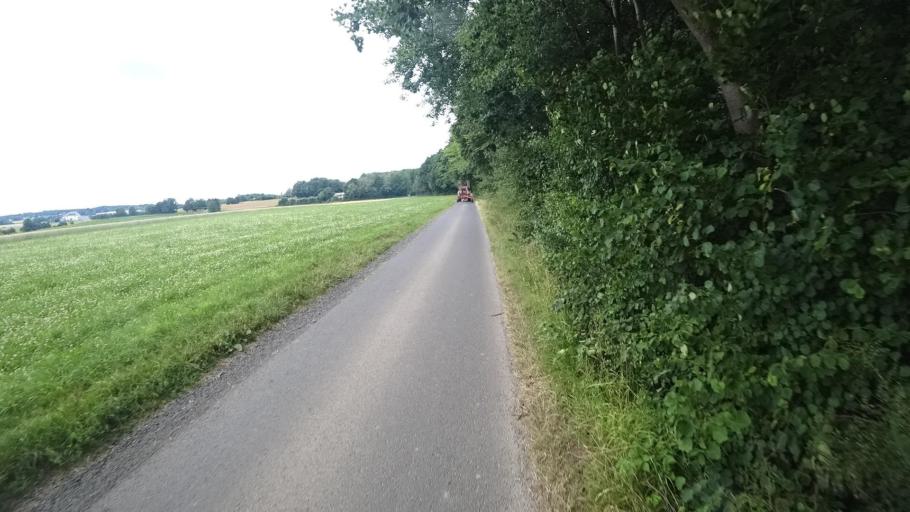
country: DE
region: Rheinland-Pfalz
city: Giershausen
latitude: 50.6779
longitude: 7.5581
